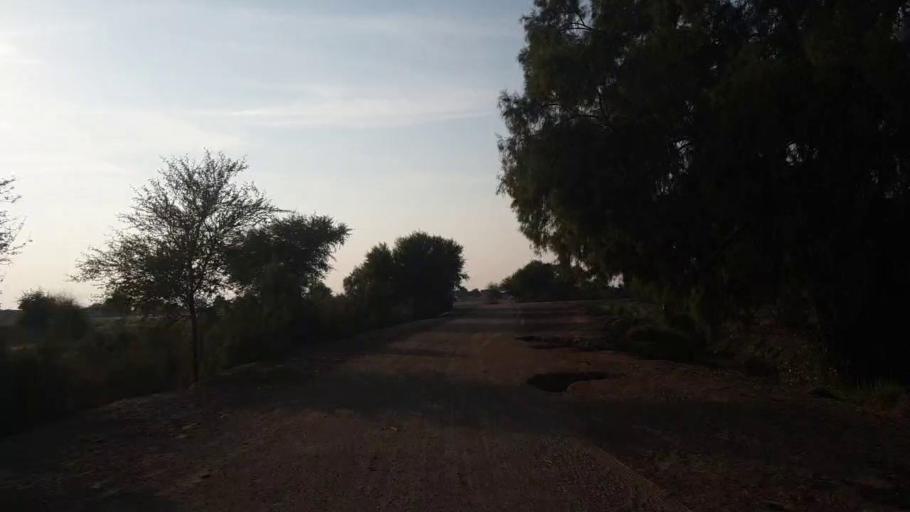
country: PK
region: Sindh
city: Sann
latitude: 25.9457
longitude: 68.1805
